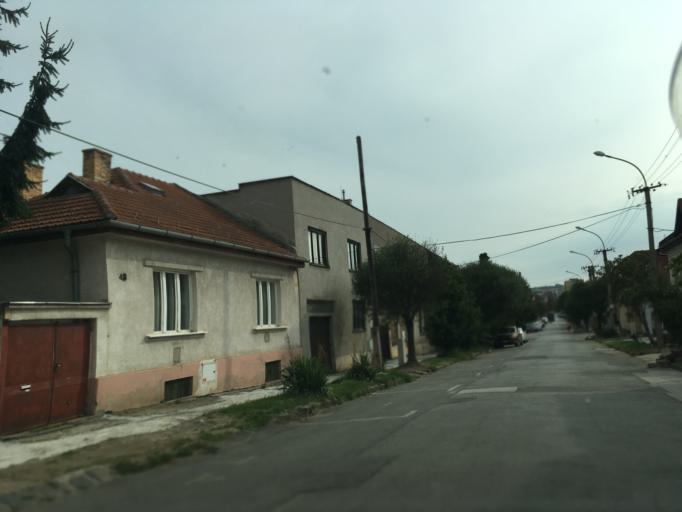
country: SK
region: Kosicky
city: Kosice
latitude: 48.7118
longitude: 21.2491
